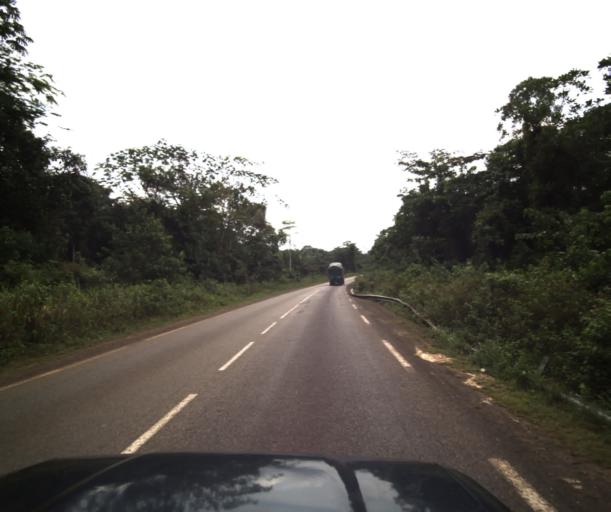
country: CM
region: Littoral
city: Edea
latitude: 3.8260
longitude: 10.3879
